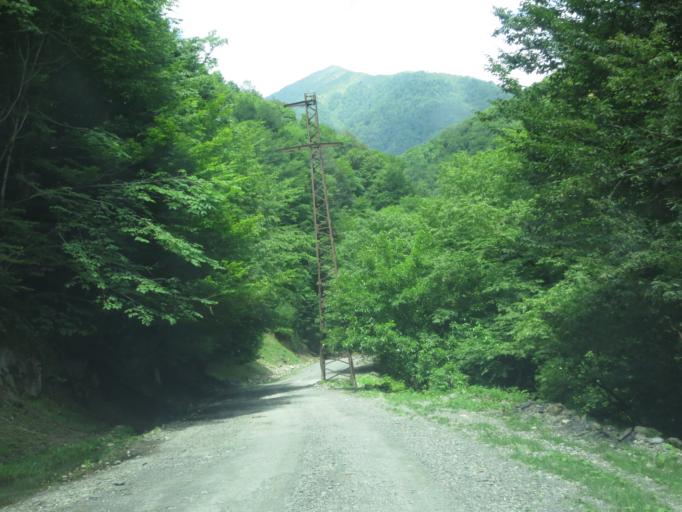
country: GE
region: Kakheti
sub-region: Telavi
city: Telavi
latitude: 42.1888
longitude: 45.4500
